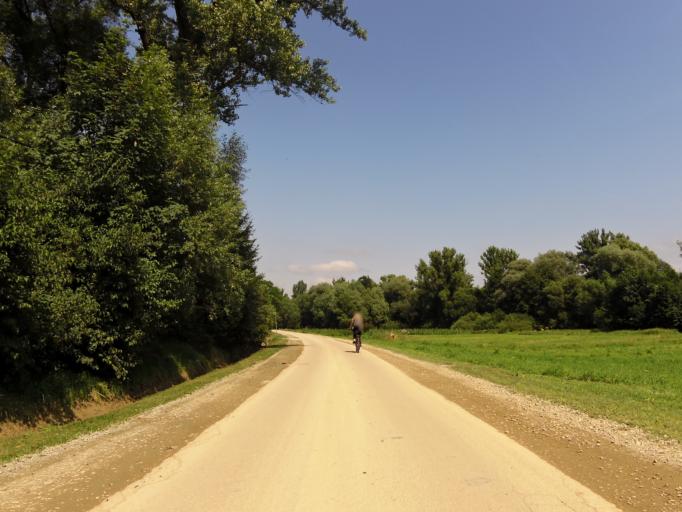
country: PL
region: Silesian Voivodeship
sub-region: Powiat zywiecki
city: Cisiec
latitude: 49.5896
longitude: 19.0965
